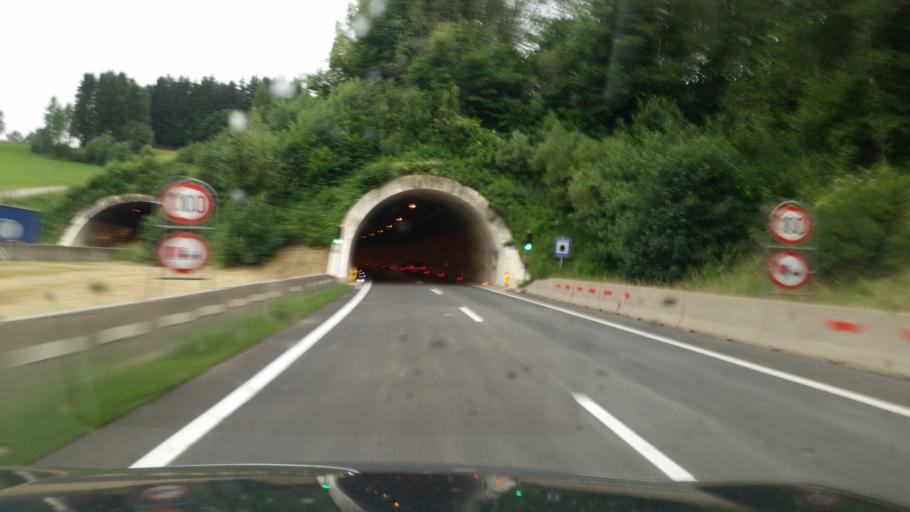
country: AT
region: Carinthia
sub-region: Politischer Bezirk Wolfsberg
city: Preitenegg
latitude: 46.9484
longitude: 14.8734
